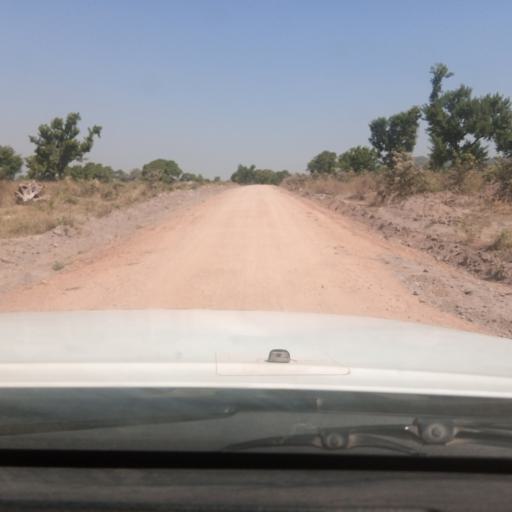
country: NG
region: Adamawa
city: Yola
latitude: 9.0529
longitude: 12.3874
